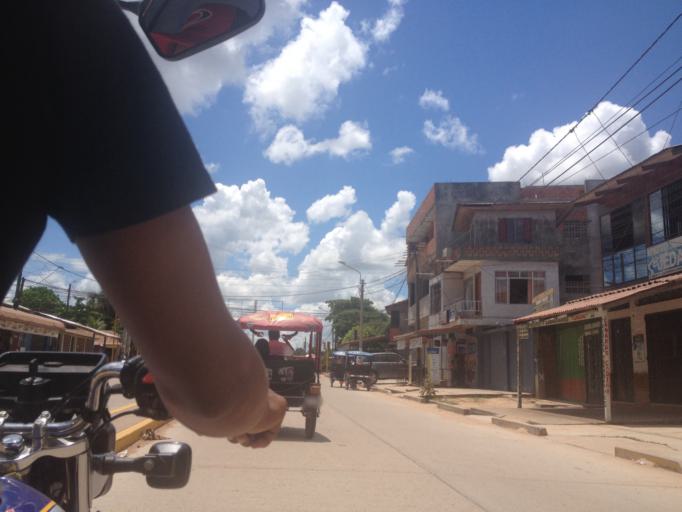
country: PE
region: Ucayali
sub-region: Provincia de Coronel Portillo
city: Pucallpa
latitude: -8.3802
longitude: -74.5563
